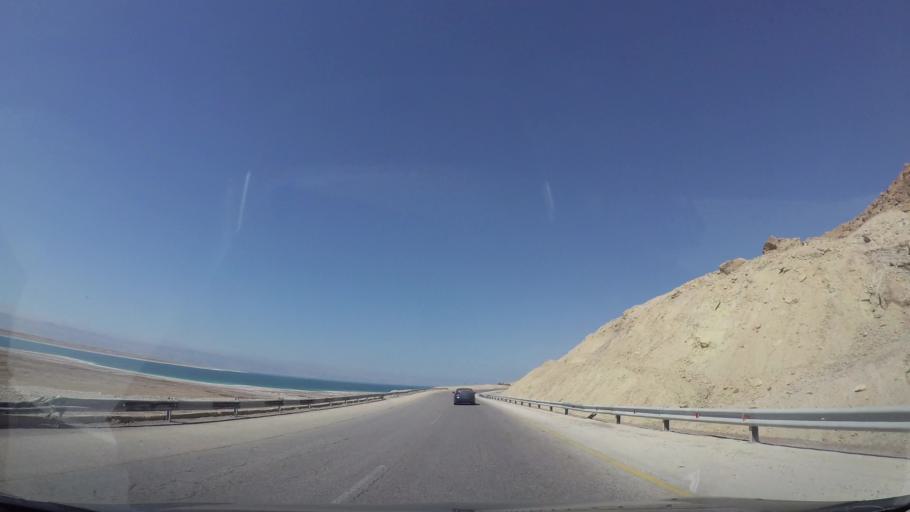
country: JO
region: Karak
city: Al Qasr
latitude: 31.3348
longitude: 35.5482
